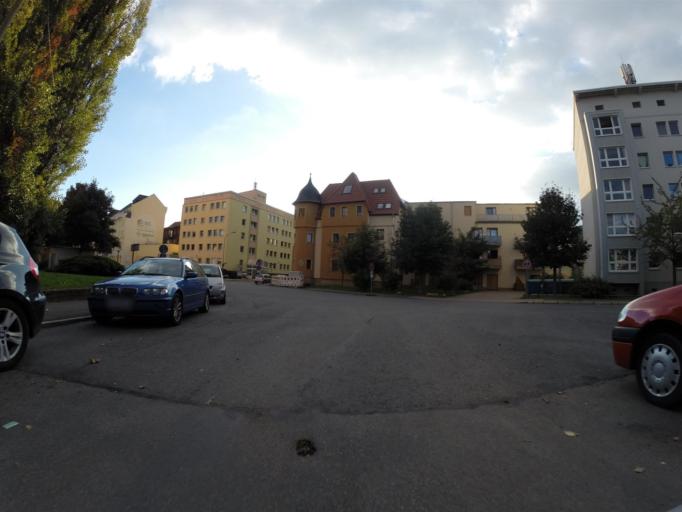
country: DE
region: Thuringia
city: Jena
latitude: 50.9361
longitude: 11.5920
